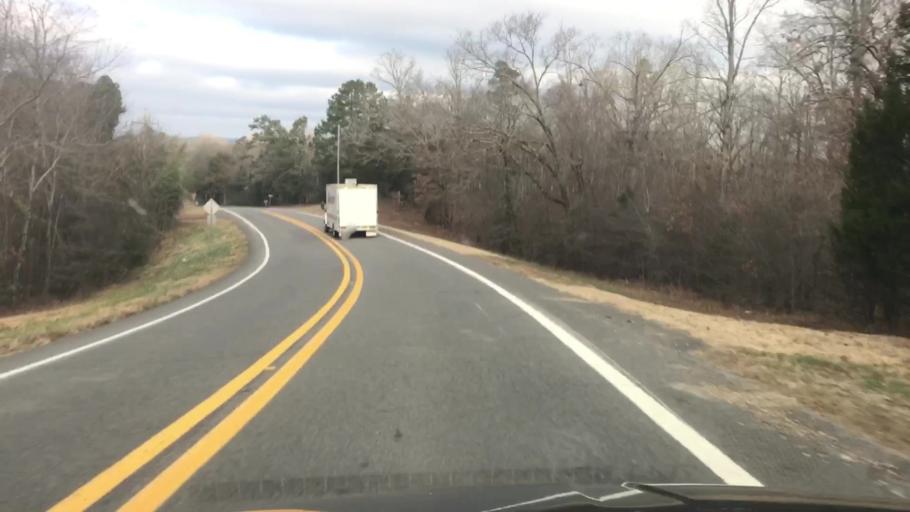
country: US
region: Arkansas
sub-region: Montgomery County
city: Mount Ida
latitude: 34.6209
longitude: -93.7231
